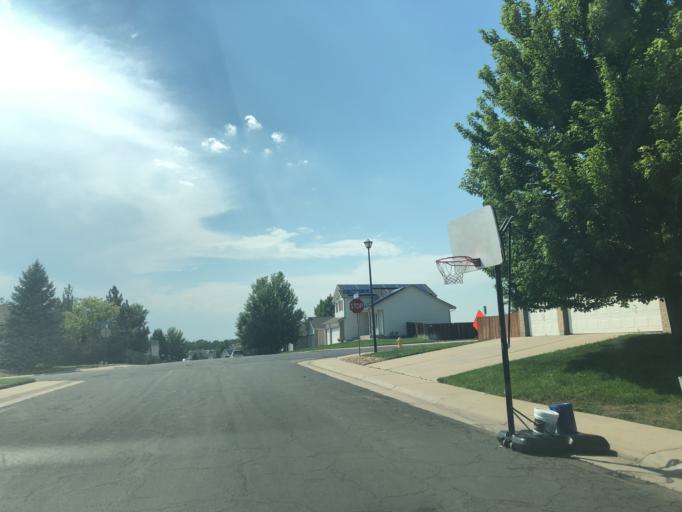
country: US
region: Colorado
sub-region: Arapahoe County
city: Dove Valley
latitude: 39.6332
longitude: -104.7590
